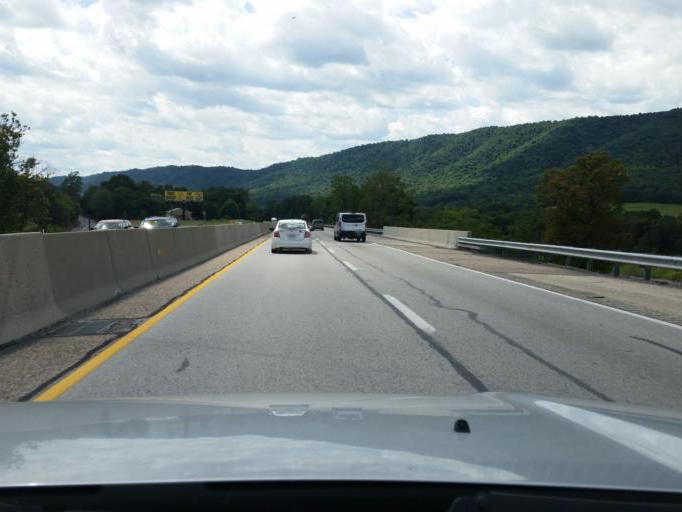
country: US
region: Pennsylvania
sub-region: Franklin County
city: Doylestown
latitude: 40.1589
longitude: -77.6972
